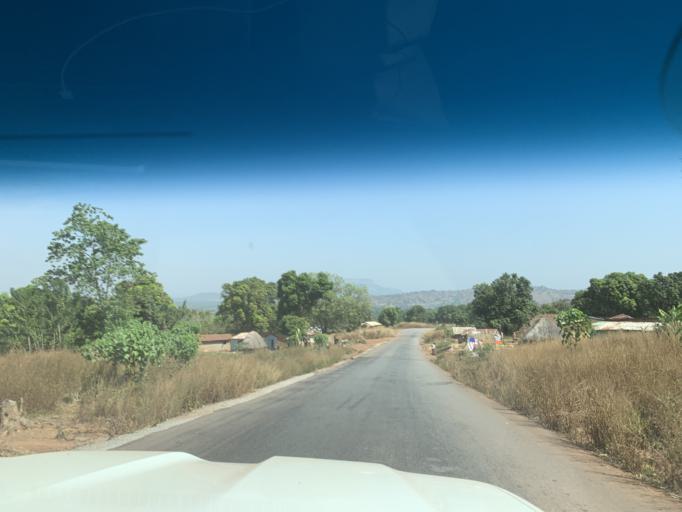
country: GN
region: Kindia
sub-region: Kindia
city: Kindia
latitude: 10.0854
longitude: -12.6419
